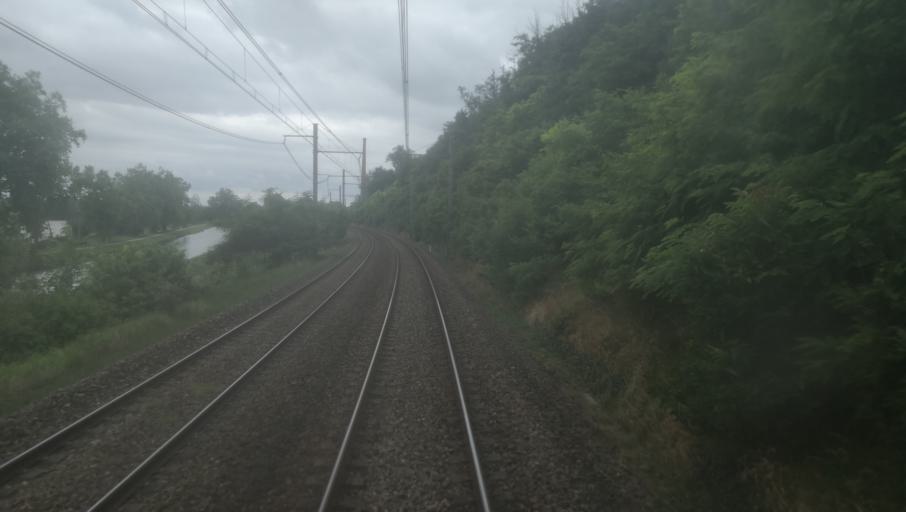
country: FR
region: Midi-Pyrenees
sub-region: Departement du Tarn-et-Garonne
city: Moissac
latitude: 44.1000
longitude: 1.0684
